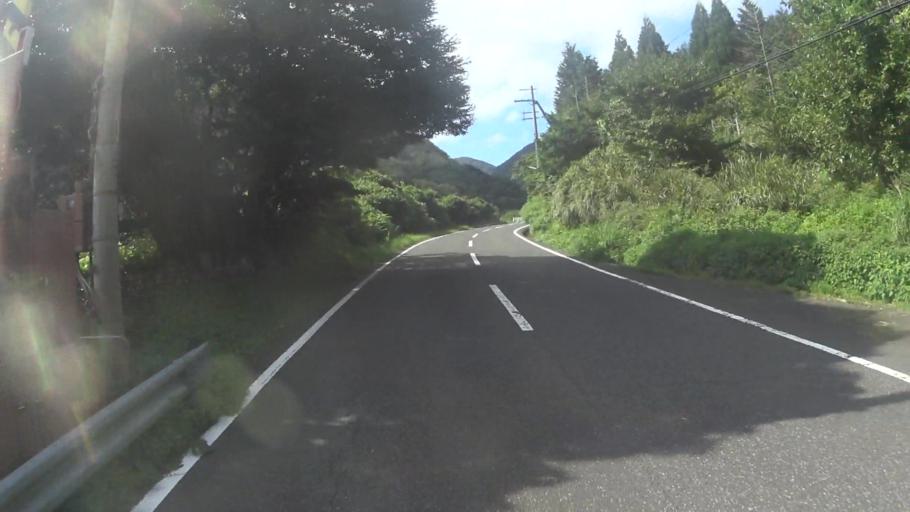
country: JP
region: Kyoto
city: Miyazu
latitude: 35.7392
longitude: 135.2466
